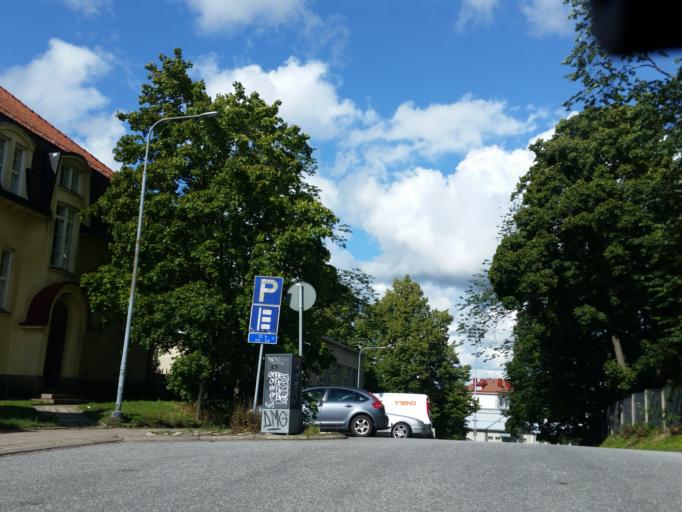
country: FI
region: Varsinais-Suomi
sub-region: Turku
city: Turku
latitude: 60.4556
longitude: 22.2729
